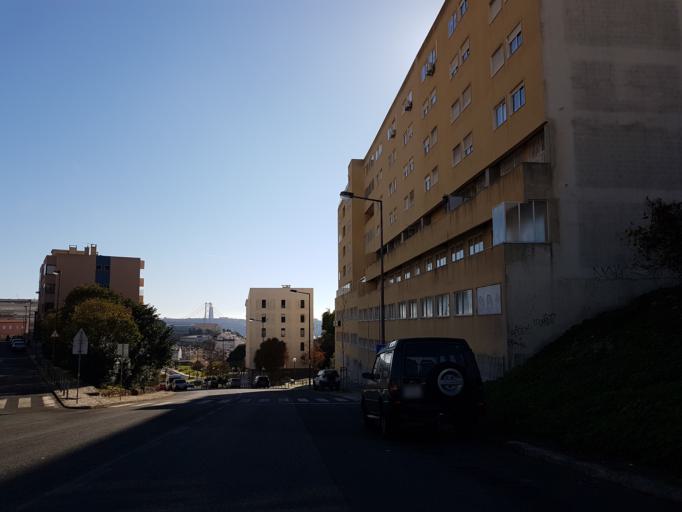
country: PT
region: Lisbon
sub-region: Oeiras
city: Alges
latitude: 38.7085
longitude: -9.1946
